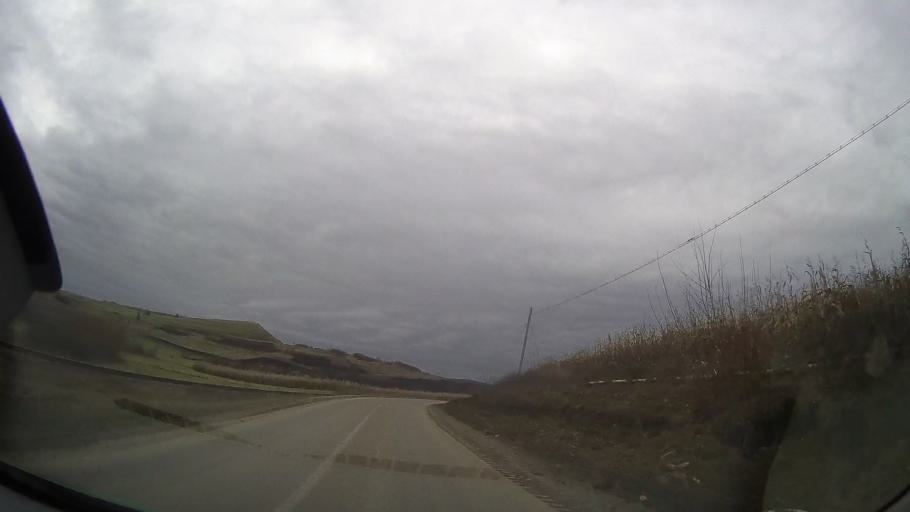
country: RO
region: Cluj
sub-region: Comuna Catina
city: Catina
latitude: 46.8131
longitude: 24.2240
